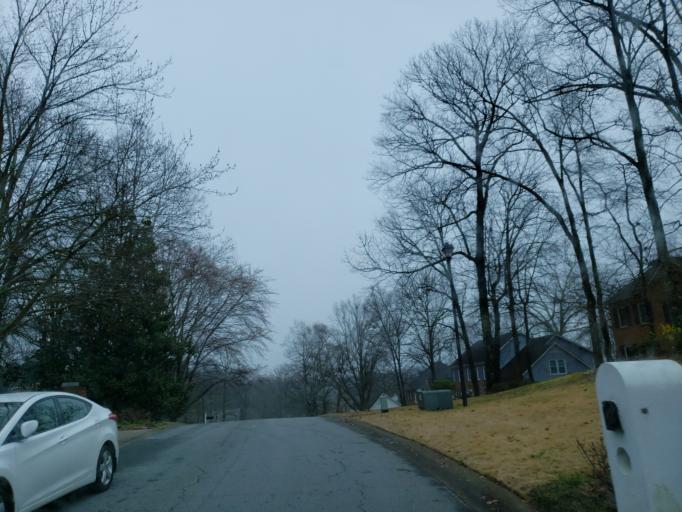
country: US
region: Georgia
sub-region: Cobb County
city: Marietta
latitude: 33.9304
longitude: -84.5770
